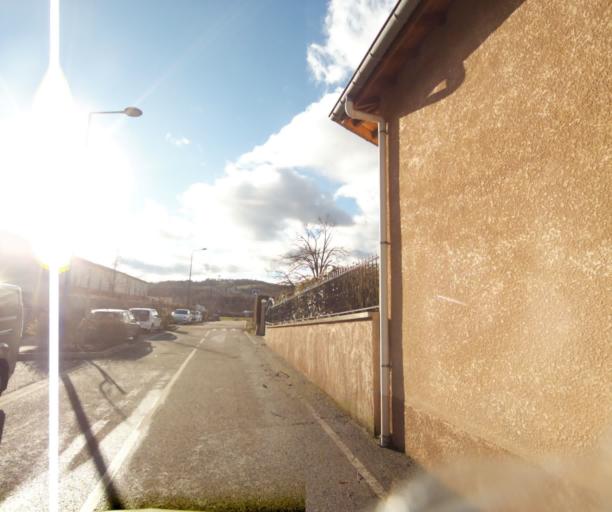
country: FR
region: Rhone-Alpes
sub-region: Departement de la Loire
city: La Talaudiere
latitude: 45.4778
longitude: 4.4328
